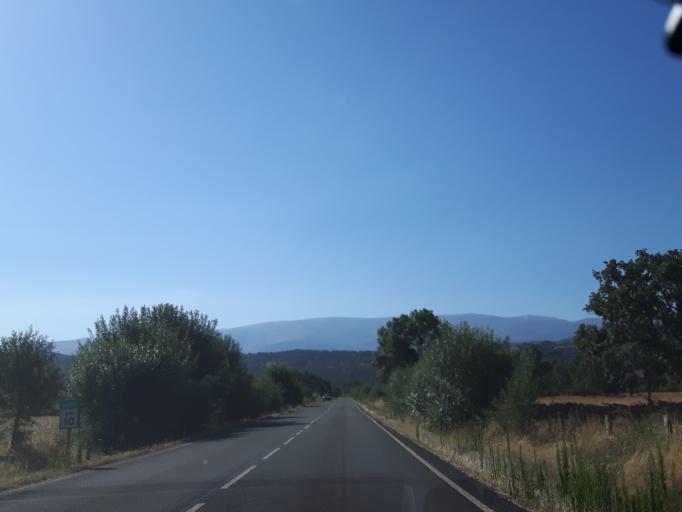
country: ES
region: Castille and Leon
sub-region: Provincia de Salamanca
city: Valdehijaderos
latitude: 40.4257
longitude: -5.8166
